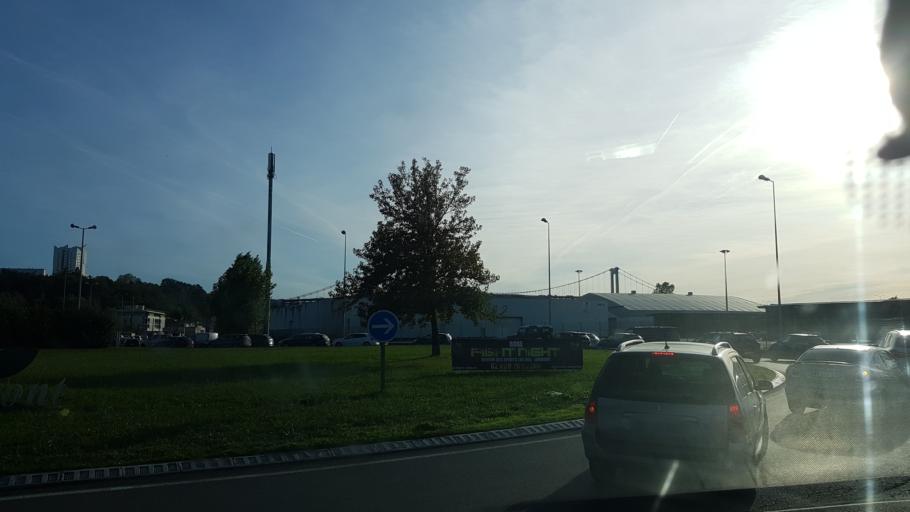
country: FR
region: Aquitaine
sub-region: Departement de la Gironde
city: Lormont
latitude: 44.8891
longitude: -0.5297
